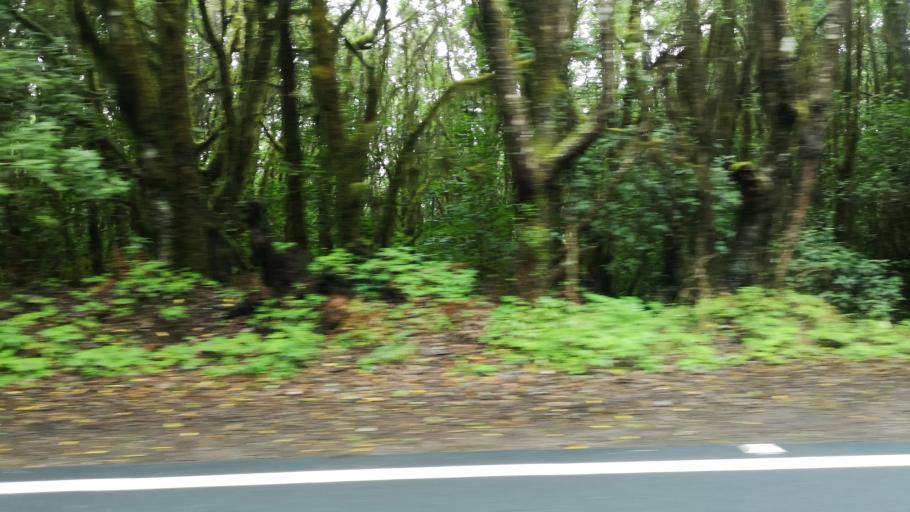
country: ES
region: Canary Islands
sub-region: Provincia de Santa Cruz de Tenerife
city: Vallehermosa
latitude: 28.1514
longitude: -17.2970
